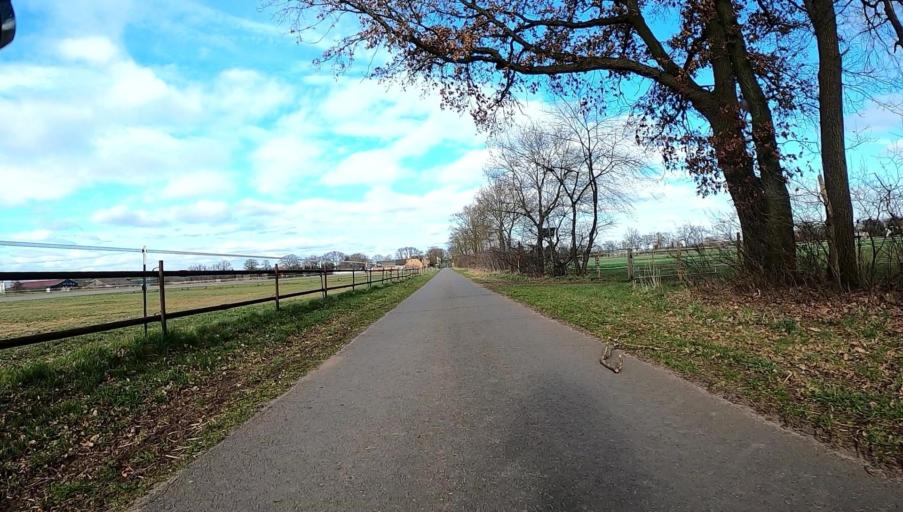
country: DE
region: Lower Saxony
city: Lindwedel
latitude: 52.6050
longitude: 9.7129
